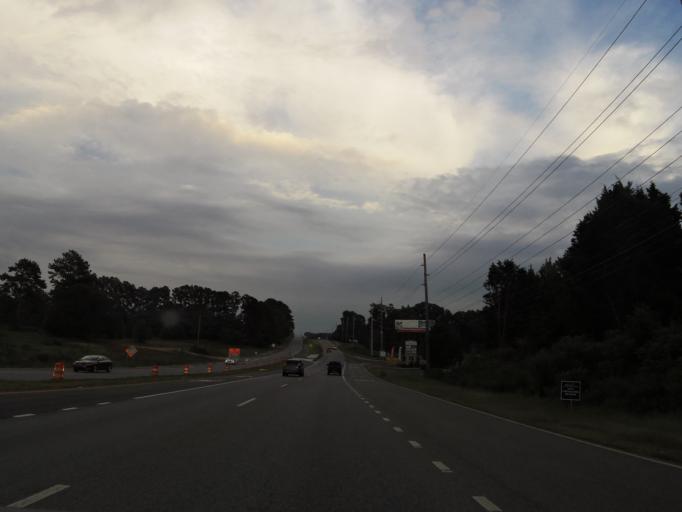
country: US
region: Alabama
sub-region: Madison County
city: Madison
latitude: 34.7533
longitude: -86.7081
